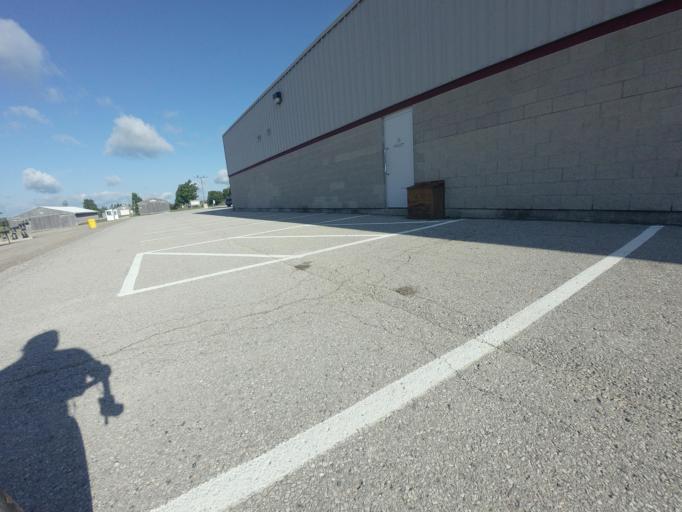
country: CA
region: Ontario
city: Huron East
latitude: 43.7363
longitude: -81.4325
